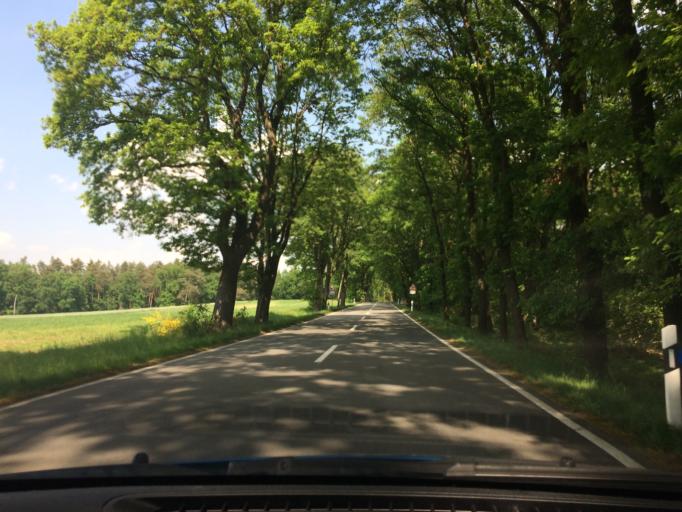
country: DE
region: Lower Saxony
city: Neu Darchau
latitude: 53.2216
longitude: 10.8622
